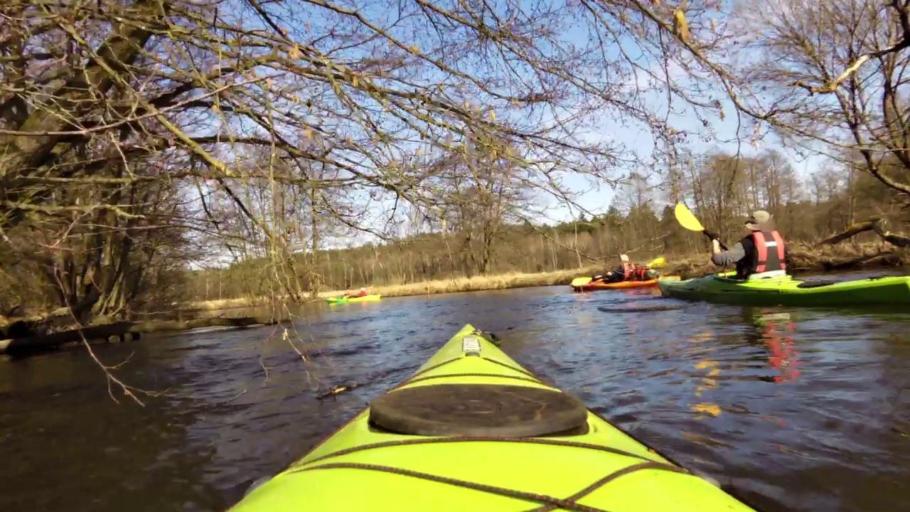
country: PL
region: West Pomeranian Voivodeship
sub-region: Powiat lobeski
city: Lobez
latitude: 53.7010
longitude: 15.5553
